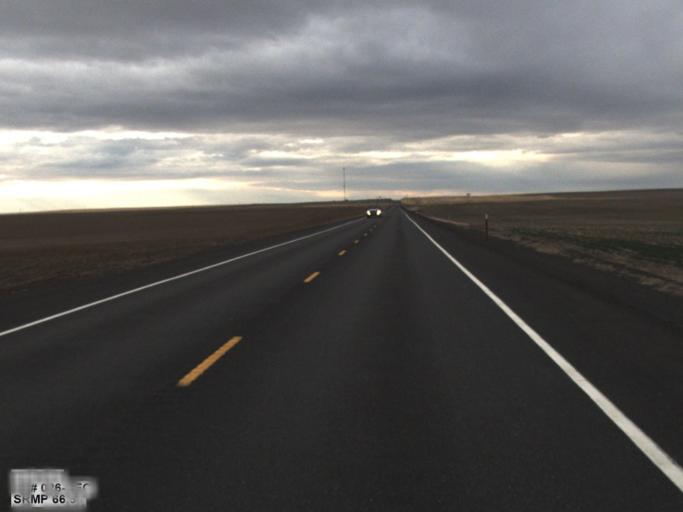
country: US
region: Washington
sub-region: Franklin County
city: Connell
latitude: 46.7945
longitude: -118.6329
